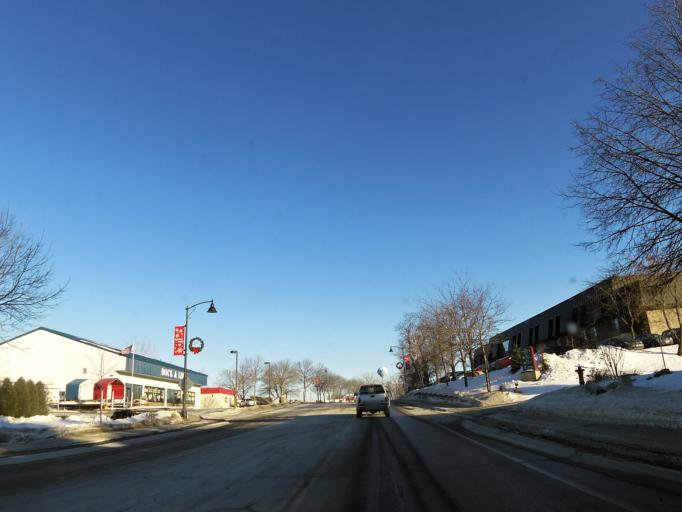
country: US
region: Minnesota
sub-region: Hennepin County
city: Spring Park
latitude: 44.9362
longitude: -93.6405
